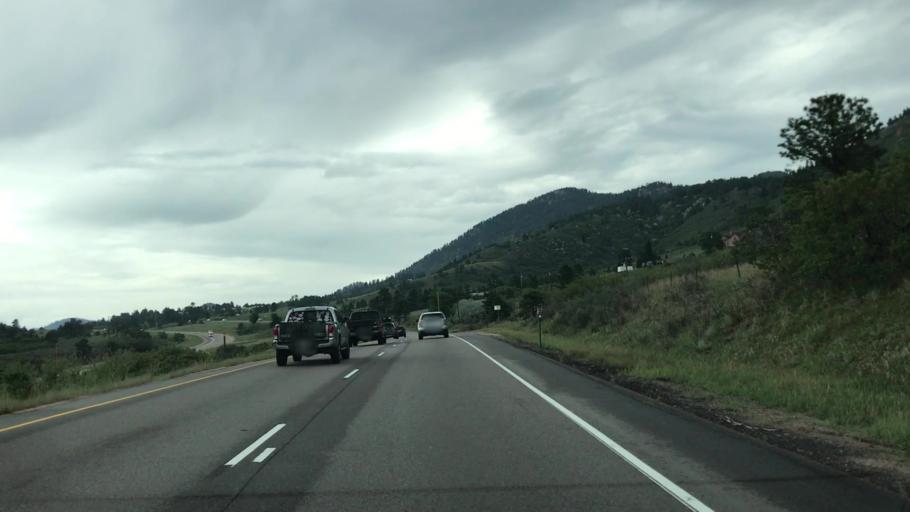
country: US
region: Colorado
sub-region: El Paso County
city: Cascade-Chipita Park
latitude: 38.9273
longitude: -104.9977
